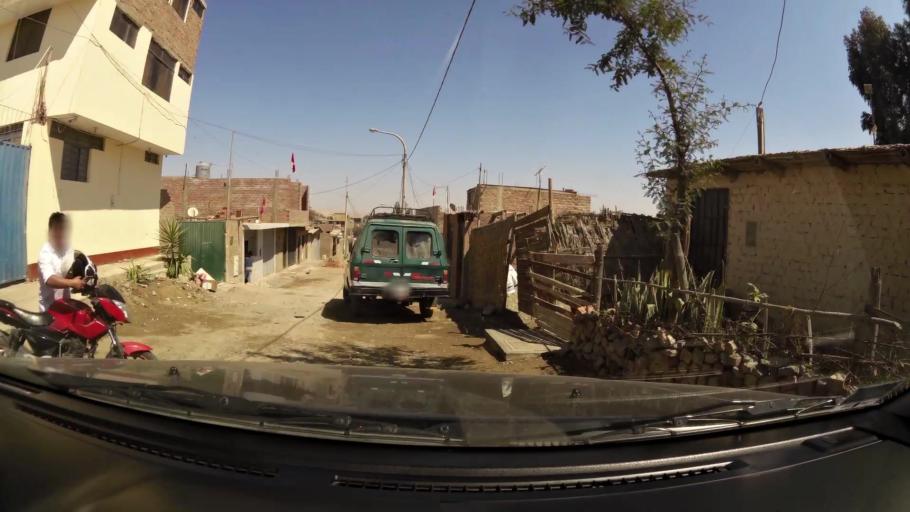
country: PE
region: Ica
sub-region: Provincia de Ica
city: Subtanjalla
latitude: -14.0415
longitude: -75.7477
